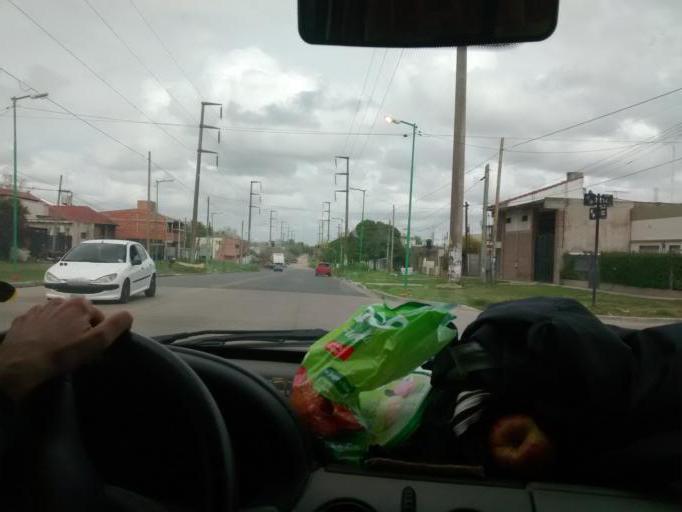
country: AR
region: Buenos Aires
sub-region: Partido de La Plata
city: La Plata
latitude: -34.9489
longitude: -57.9847
